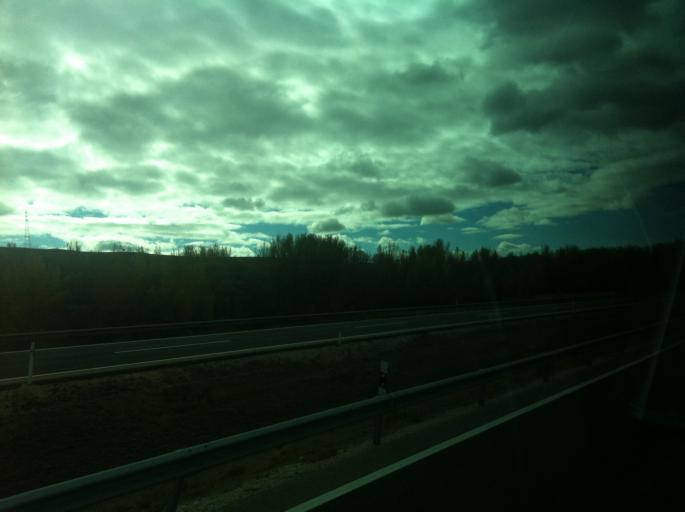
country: ES
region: Castille and Leon
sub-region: Provincia de Burgos
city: Pradanos de Bureba
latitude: 42.5017
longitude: -3.3537
